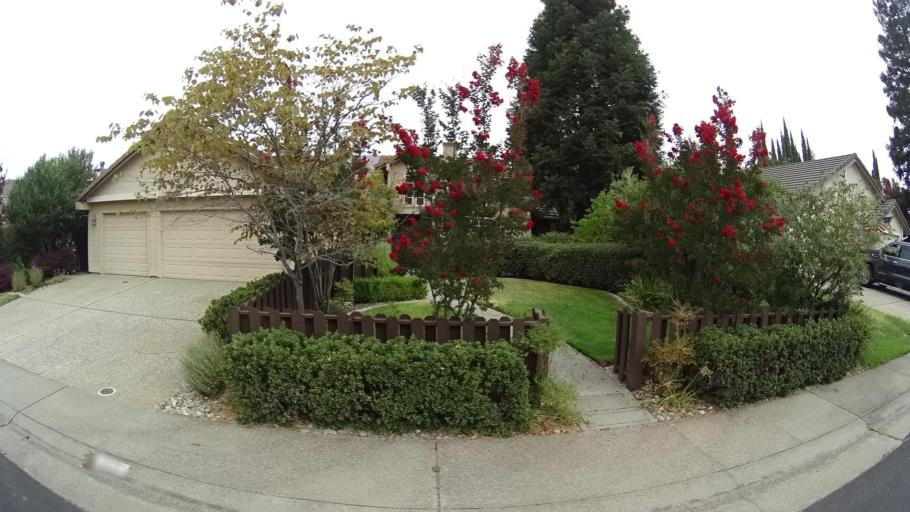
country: US
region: California
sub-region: Placer County
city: Rocklin
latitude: 38.7817
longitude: -121.2069
